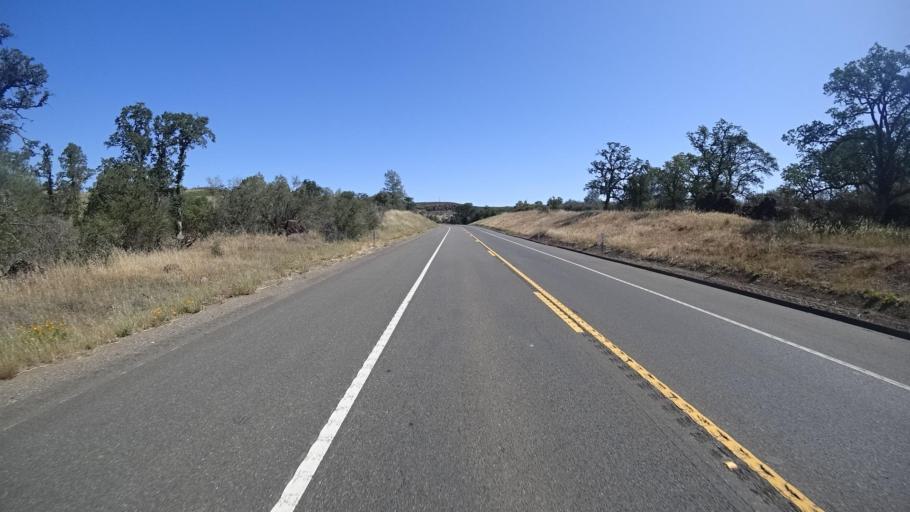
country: US
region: California
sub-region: Lake County
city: Clearlake
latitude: 38.9992
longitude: -122.6057
